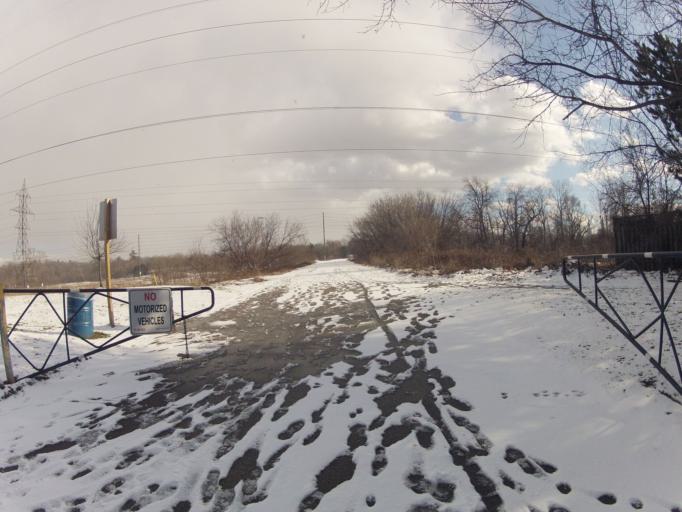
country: CA
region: Ontario
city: Mississauga
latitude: 43.5672
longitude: -79.6816
